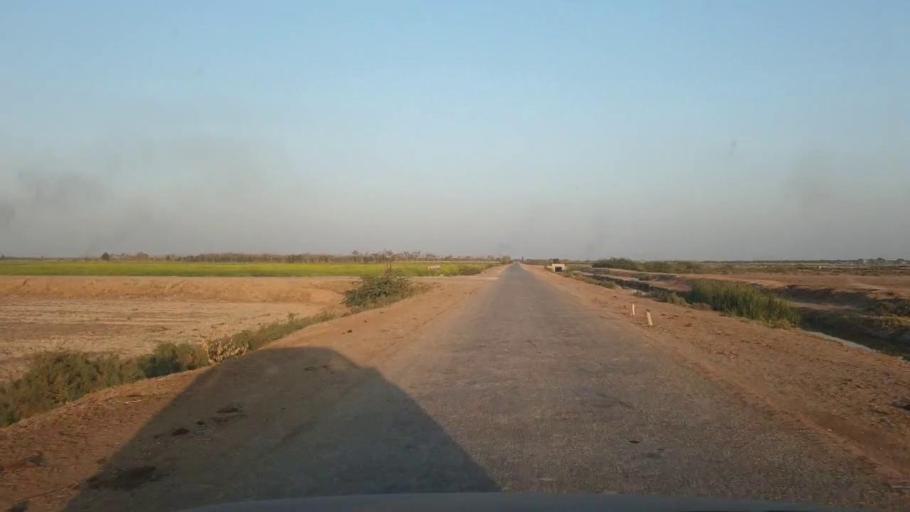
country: PK
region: Sindh
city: Chambar
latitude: 25.2784
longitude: 68.9288
